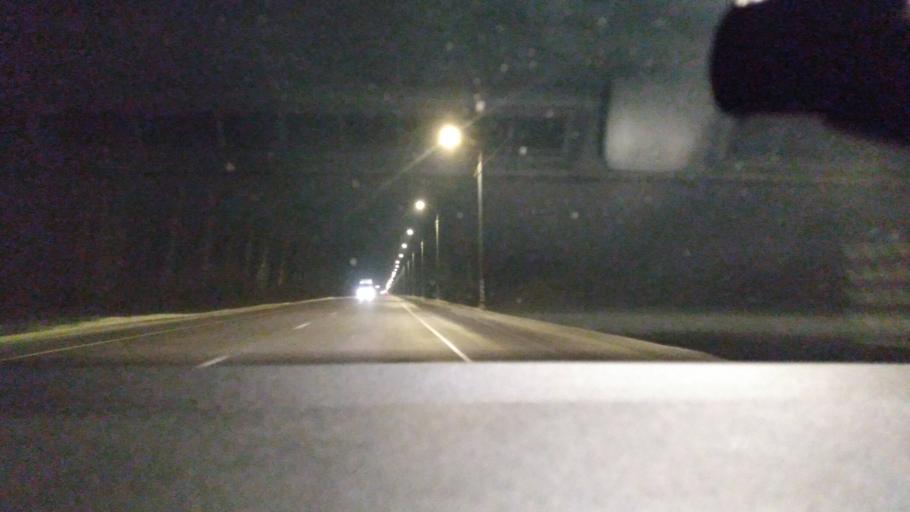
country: RU
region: Moskovskaya
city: Yegor'yevsk
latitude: 55.4513
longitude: 39.0029
